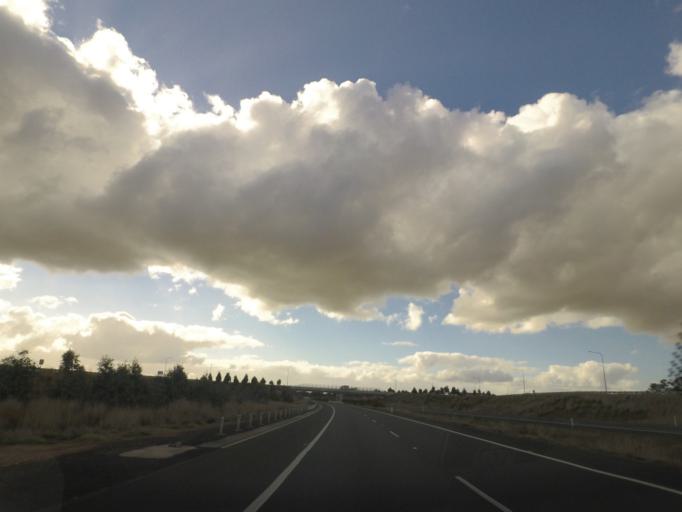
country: AU
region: New South Wales
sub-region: Greater Hume Shire
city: Holbrook
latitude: -35.7349
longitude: 147.3053
